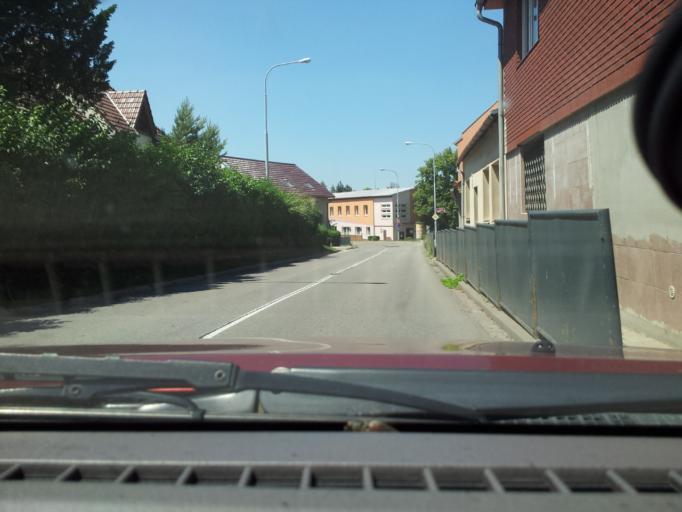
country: CZ
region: South Moravian
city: Modrice
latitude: 49.1518
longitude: 16.6563
